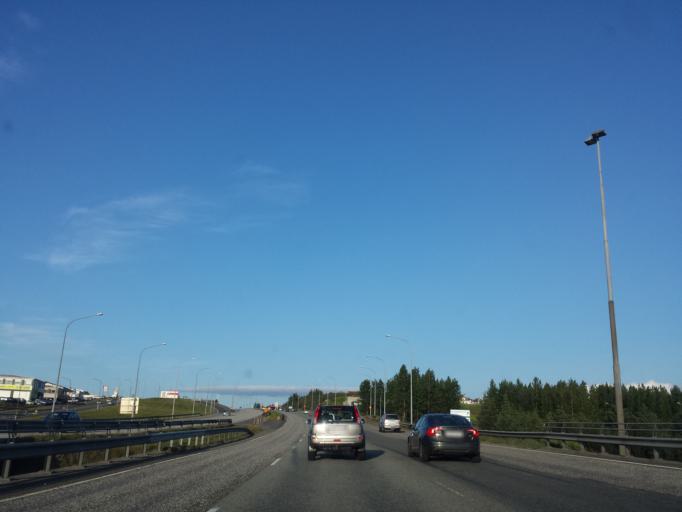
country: IS
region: Capital Region
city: Reykjavik
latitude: 64.1241
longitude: -21.8406
